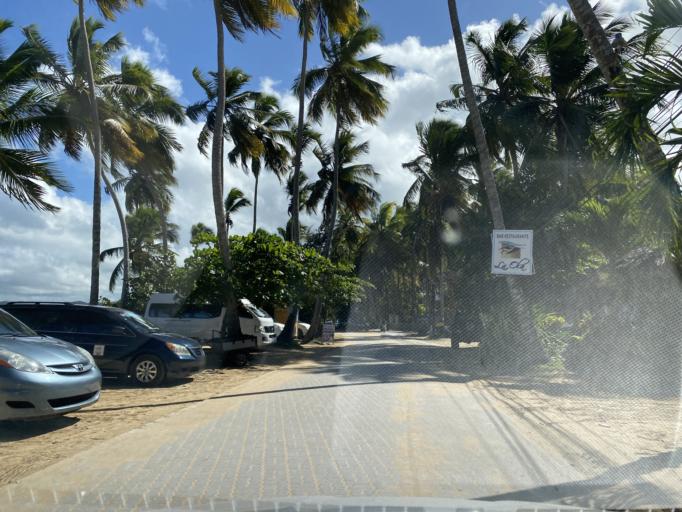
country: DO
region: Samana
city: Las Terrenas
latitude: 19.3261
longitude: -69.5447
